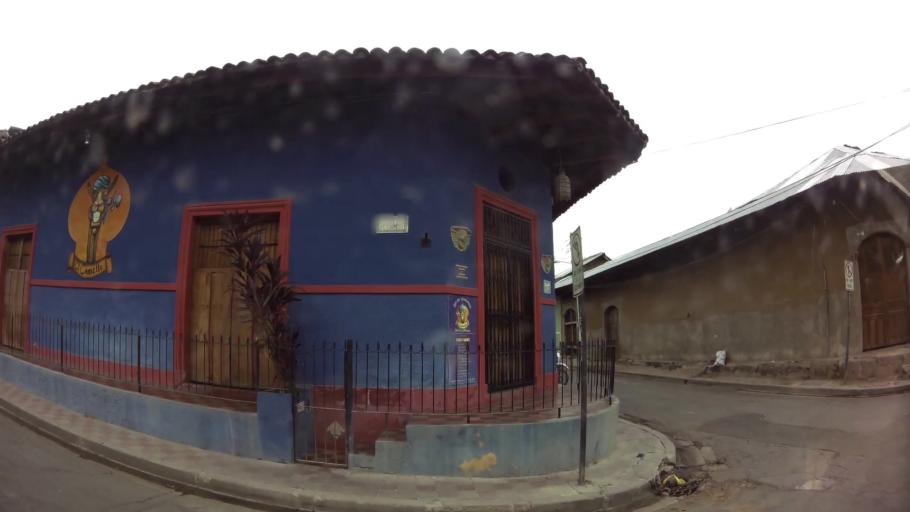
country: NI
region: Granada
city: Granada
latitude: 11.9291
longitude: -85.9515
